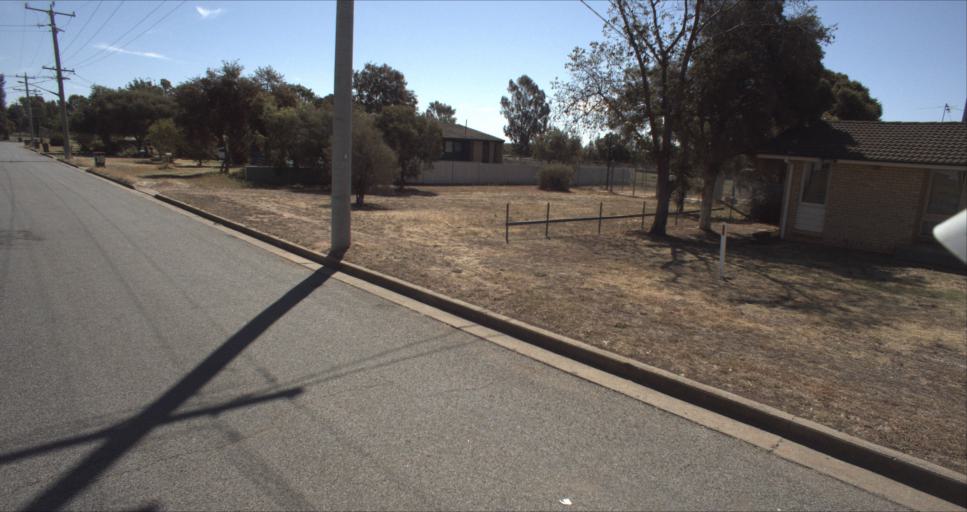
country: AU
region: New South Wales
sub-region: Leeton
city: Leeton
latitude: -34.5481
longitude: 146.3752
